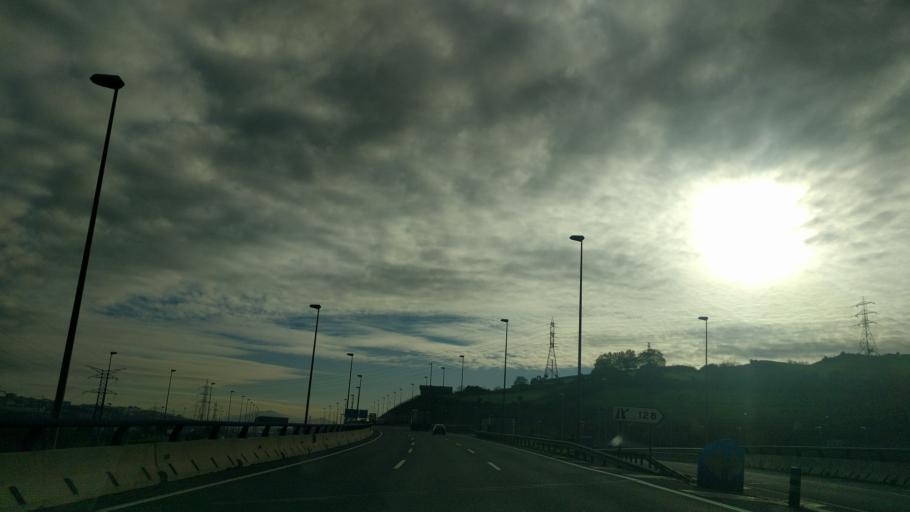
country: ES
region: Basque Country
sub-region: Bizkaia
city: Urtuella
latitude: 43.3153
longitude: -3.0471
